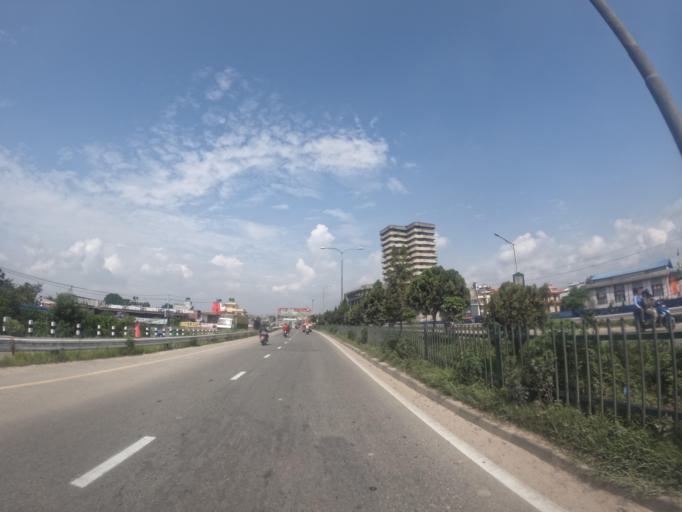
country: NP
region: Central Region
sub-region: Bagmati Zone
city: Bhaktapur
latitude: 27.6742
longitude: 85.3995
